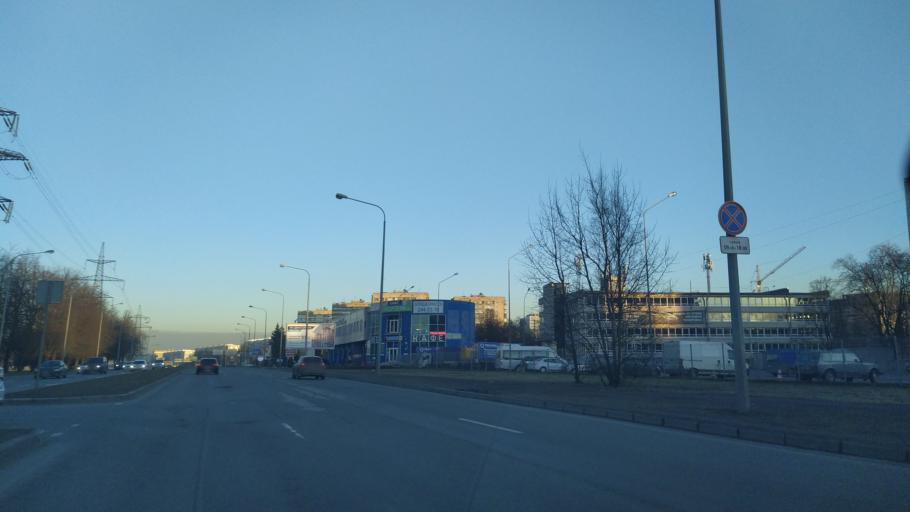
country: RU
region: Leningrad
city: Kalininskiy
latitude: 59.9756
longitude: 30.4103
